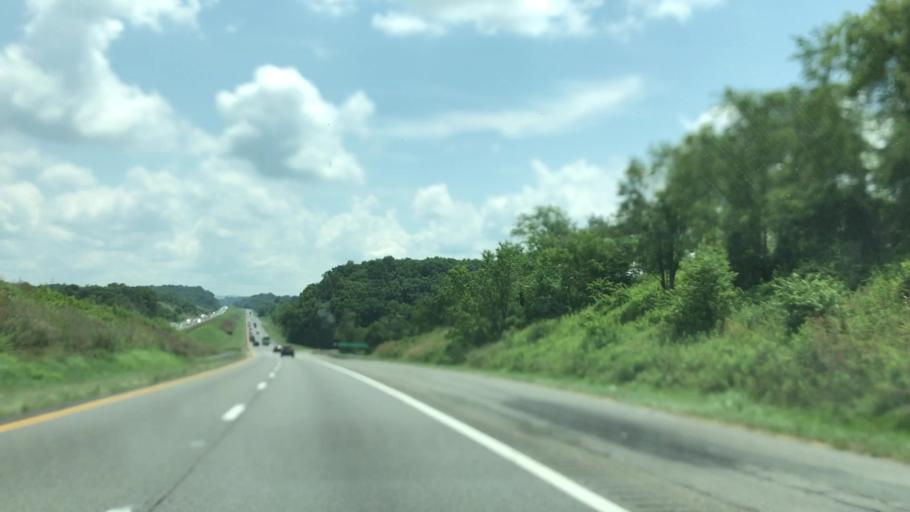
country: US
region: Virginia
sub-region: Wythe County
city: Wytheville
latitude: 36.9313
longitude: -80.9115
